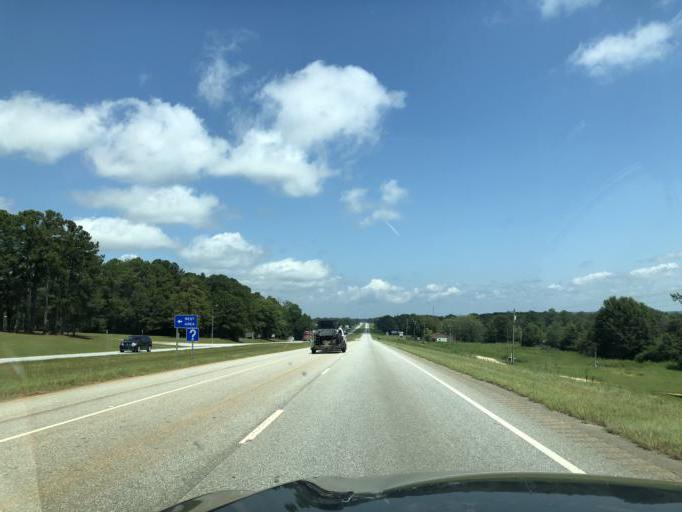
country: US
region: Alabama
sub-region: Barbour County
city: Eufaula
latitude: 31.7812
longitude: -85.1756
